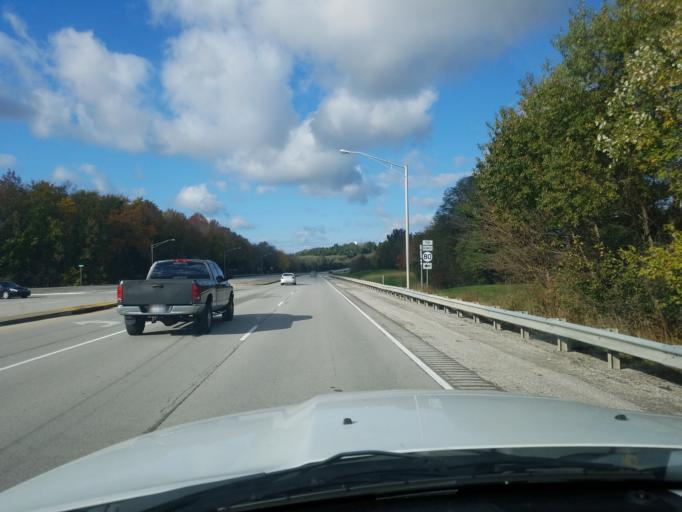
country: US
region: Kentucky
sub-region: Pulaski County
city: Somerset
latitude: 37.0933
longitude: -84.6382
